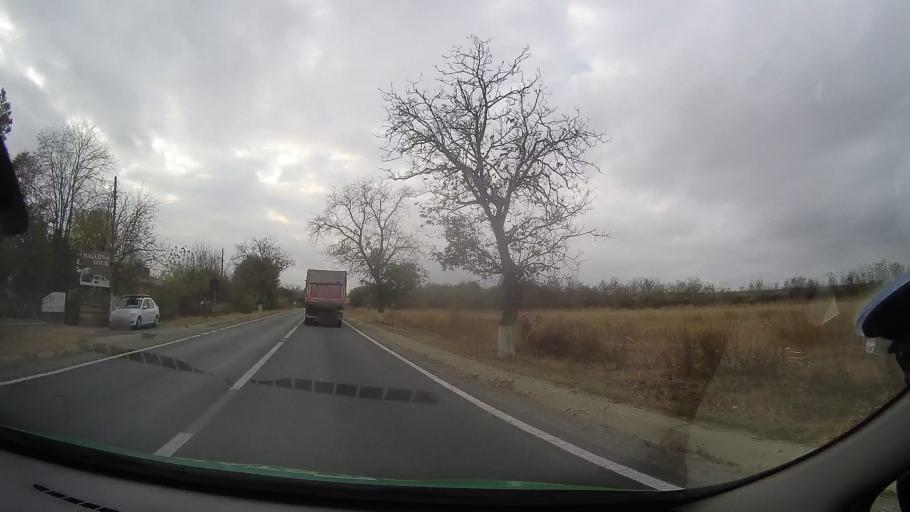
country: RO
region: Constanta
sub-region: Municipiul Medgidia
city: Medgidia
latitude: 44.2677
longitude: 28.2627
